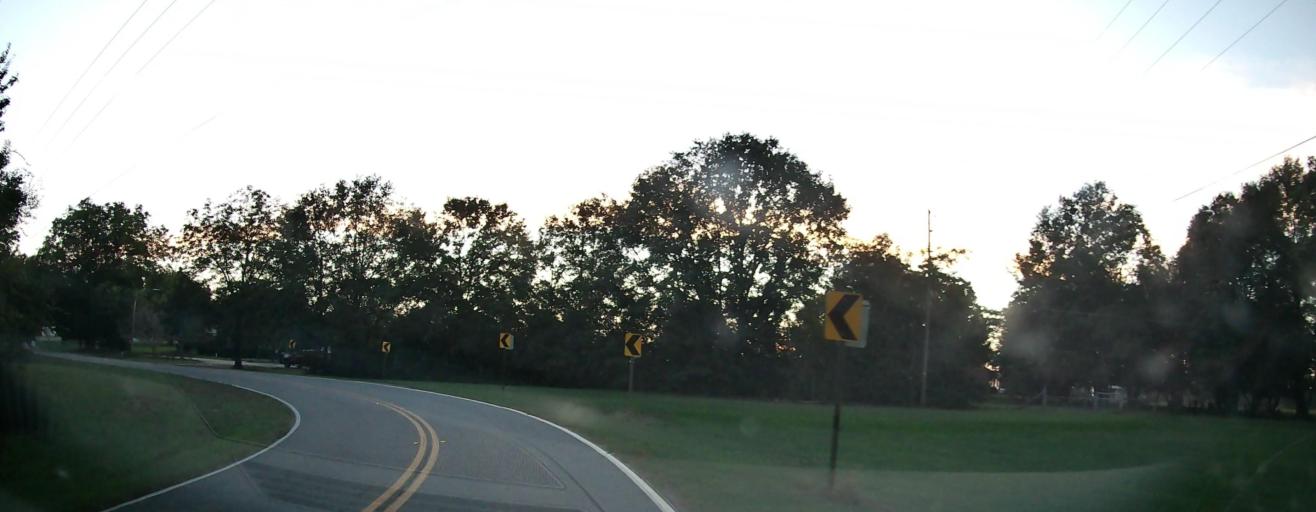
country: US
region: Georgia
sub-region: Houston County
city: Centerville
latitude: 32.6451
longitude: -83.6988
